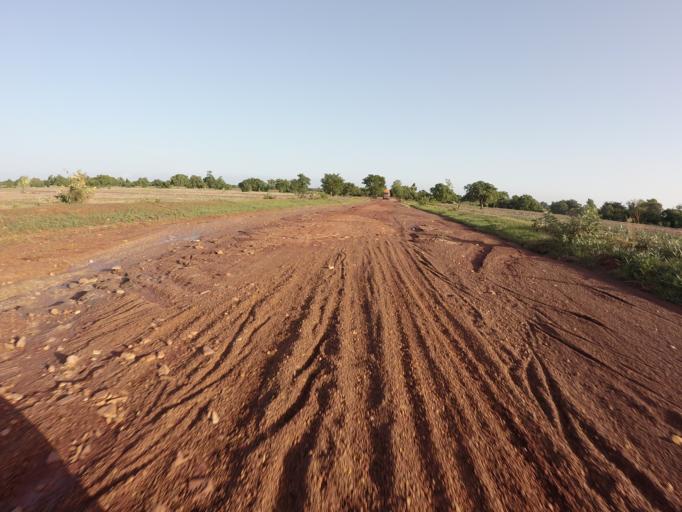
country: TG
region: Savanes
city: Sansanne-Mango
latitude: 10.3497
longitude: -0.0929
